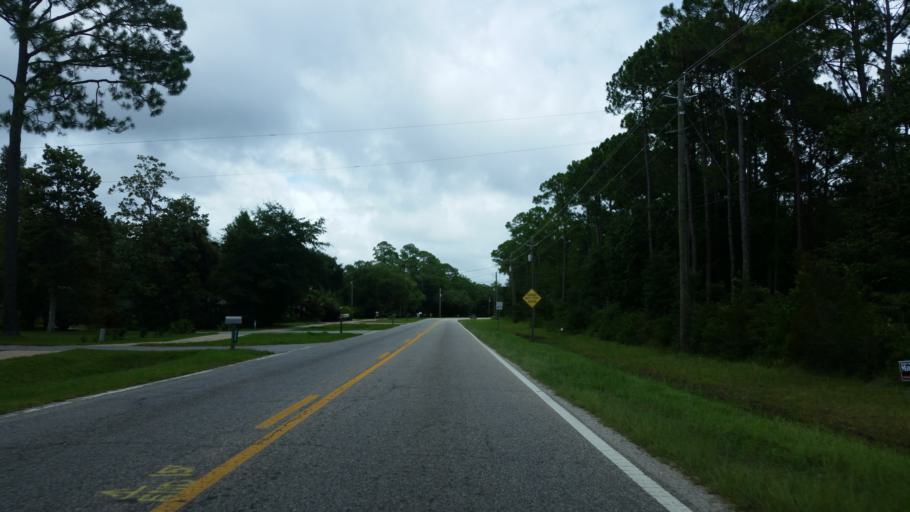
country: US
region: Florida
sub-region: Santa Rosa County
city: Holley
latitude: 30.4443
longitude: -86.9480
